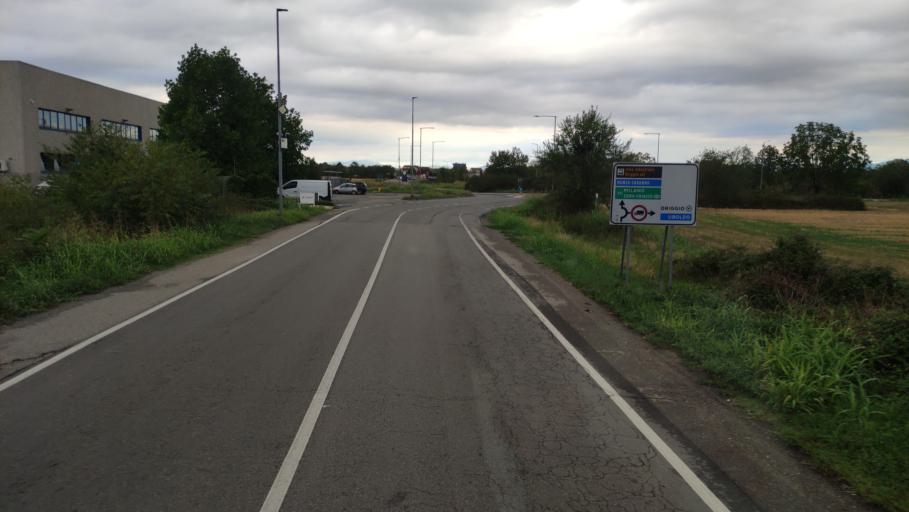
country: IT
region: Lombardy
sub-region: Provincia di Varese
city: Origgio
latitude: 45.6014
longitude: 9.0075
